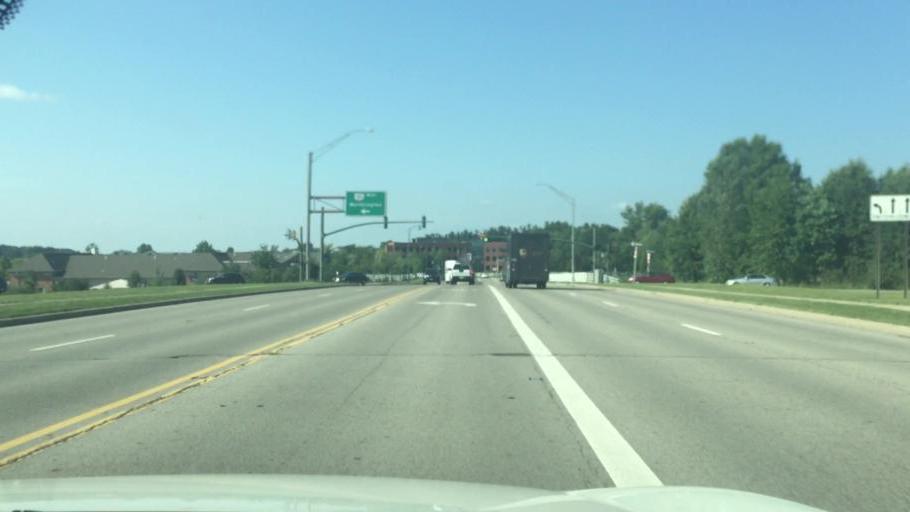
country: US
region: Ohio
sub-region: Franklin County
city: New Albany
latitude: 40.0918
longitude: -82.8230
